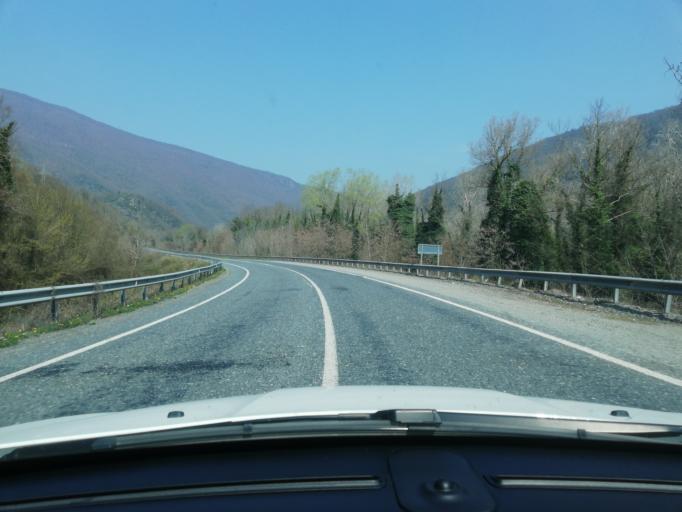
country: TR
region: Zonguldak
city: Gokcebey
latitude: 41.2523
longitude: 32.1628
